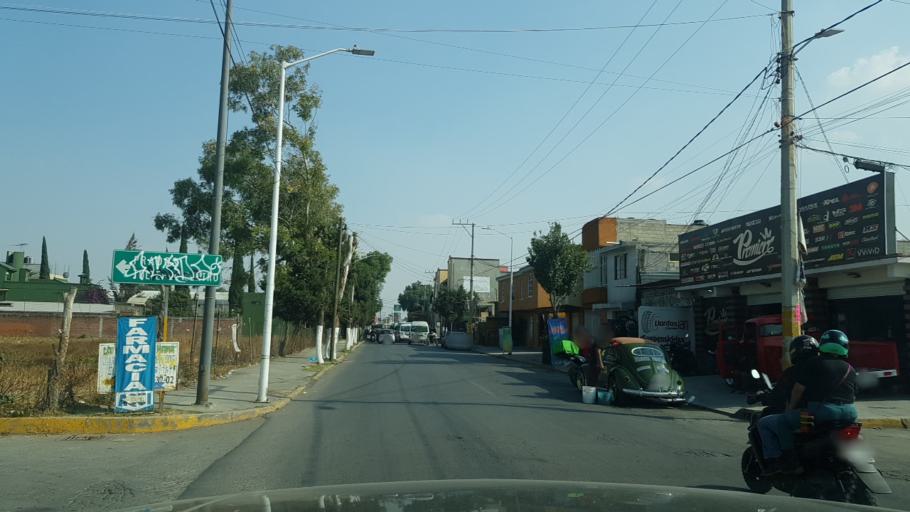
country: MX
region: Mexico
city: Santiago Teyahualco
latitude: 19.6580
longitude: -99.1257
